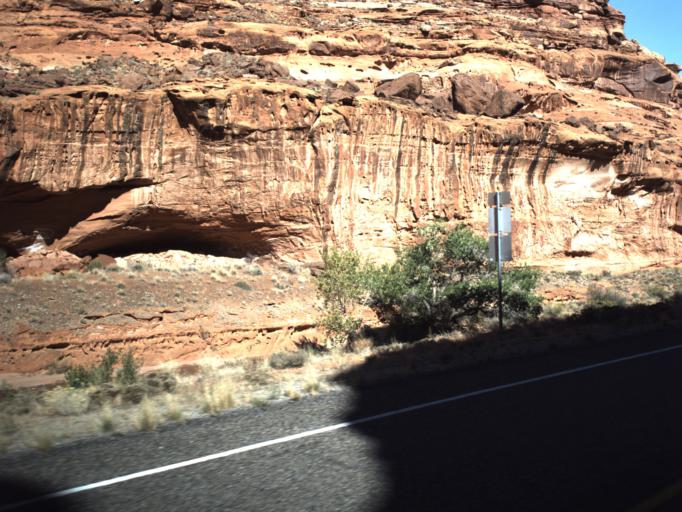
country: US
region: Utah
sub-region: San Juan County
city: Blanding
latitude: 37.9700
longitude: -110.4918
